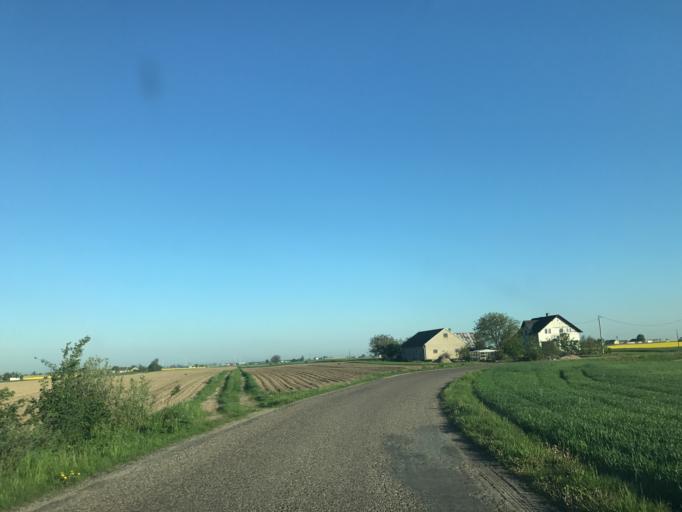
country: PL
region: Kujawsko-Pomorskie
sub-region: Powiat brodnicki
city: Gorzno
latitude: 53.1979
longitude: 19.5994
